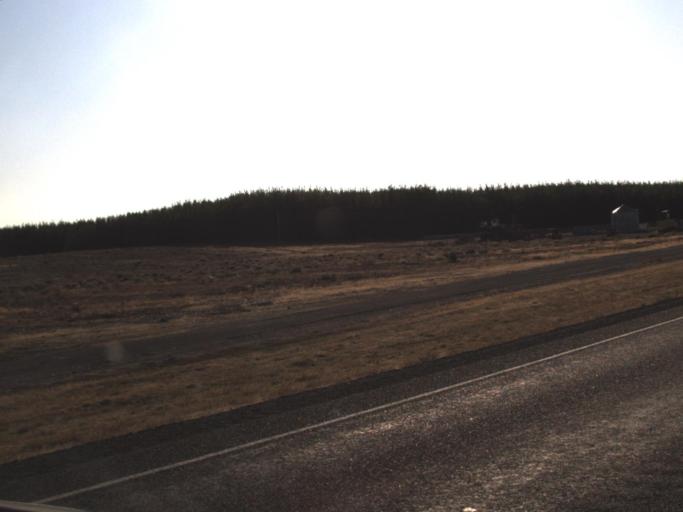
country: US
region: Washington
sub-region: Walla Walla County
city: Burbank
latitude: 46.2151
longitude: -118.8934
